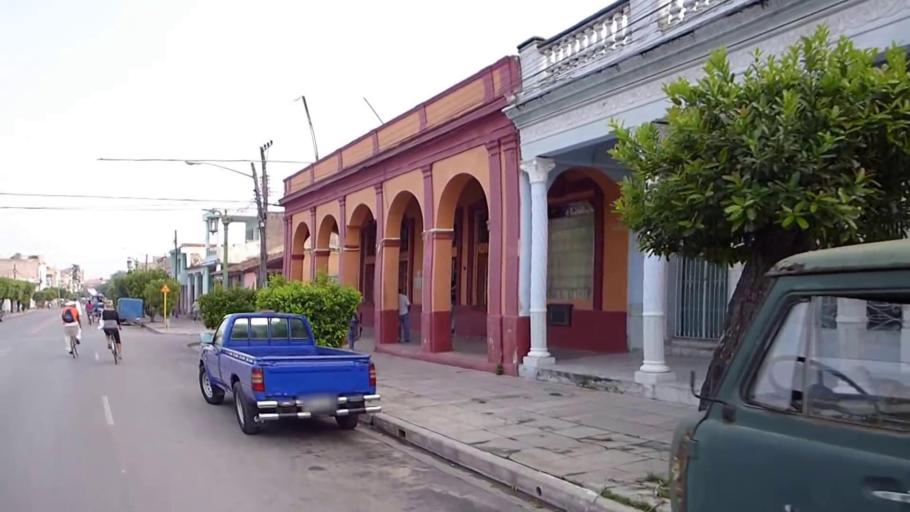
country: CU
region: Camaguey
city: Camaguey
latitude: 21.3715
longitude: -77.9090
